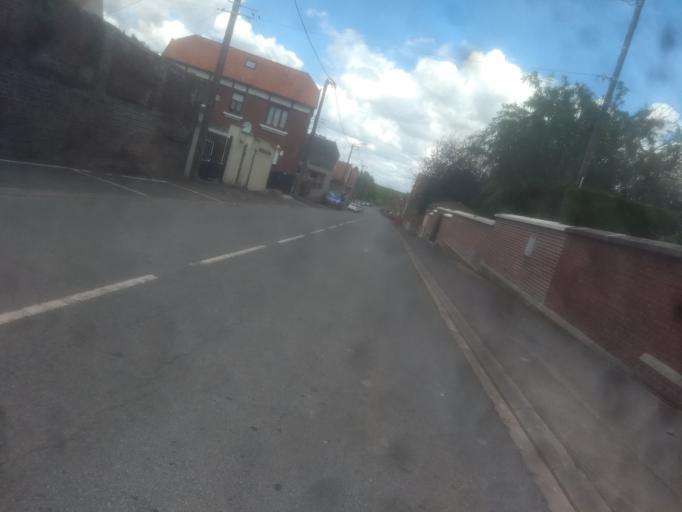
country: FR
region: Nord-Pas-de-Calais
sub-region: Departement du Pas-de-Calais
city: Beaurains
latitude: 50.2132
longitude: 2.8199
